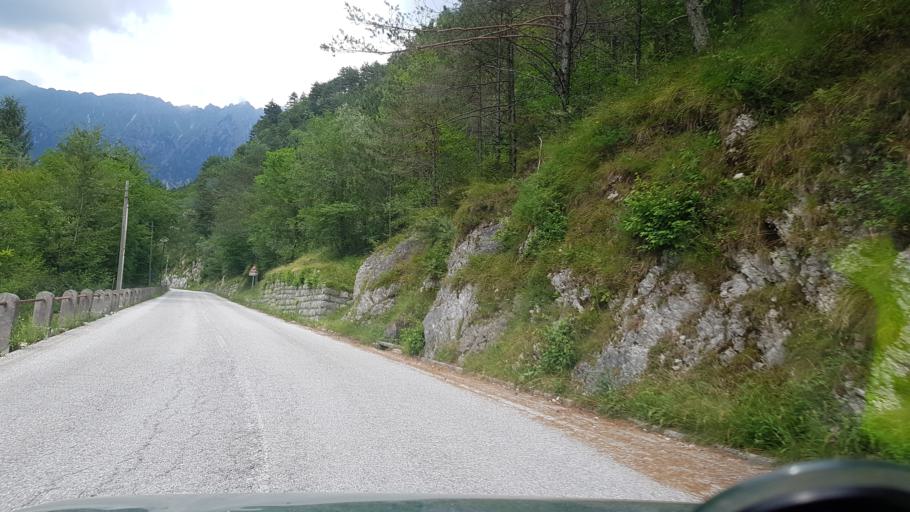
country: IT
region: Friuli Venezia Giulia
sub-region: Provincia di Udine
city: Lusevera
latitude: 46.2905
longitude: 13.2702
